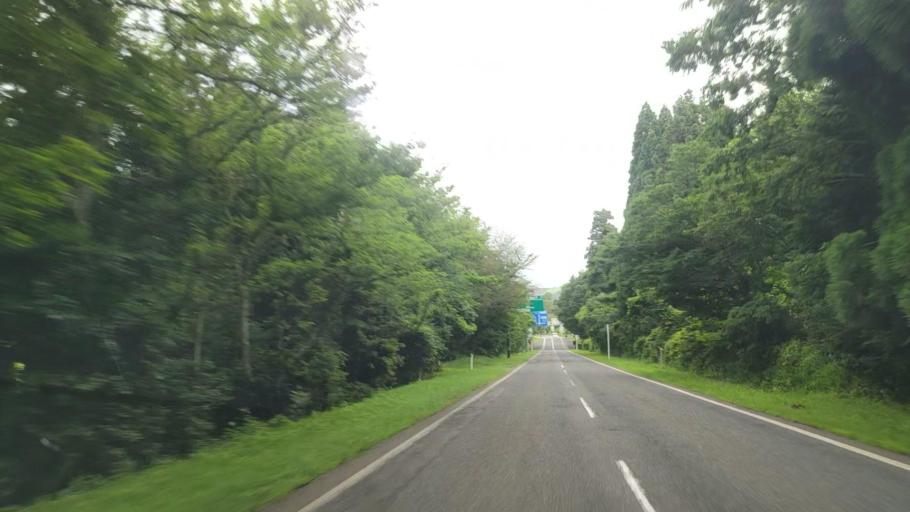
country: JP
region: Tottori
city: Yonago
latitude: 35.4065
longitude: 133.4818
